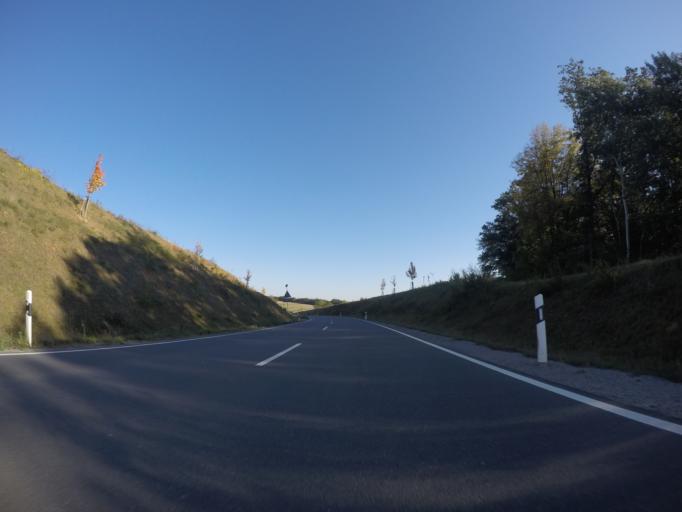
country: DE
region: Bavaria
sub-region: Regierungsbezirk Unterfranken
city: Marktheidenfeld
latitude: 49.8537
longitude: 9.5906
